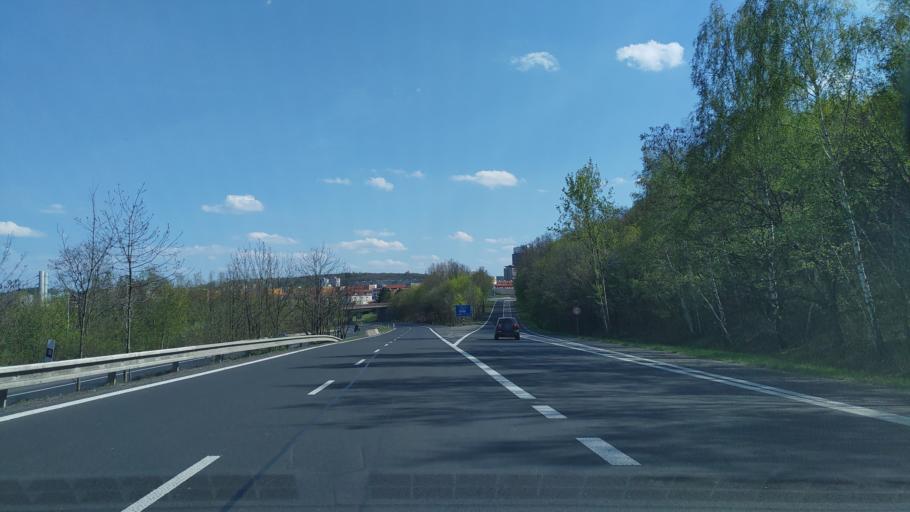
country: CZ
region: Ustecky
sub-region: Okres Most
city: Most
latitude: 50.5200
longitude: 13.6391
